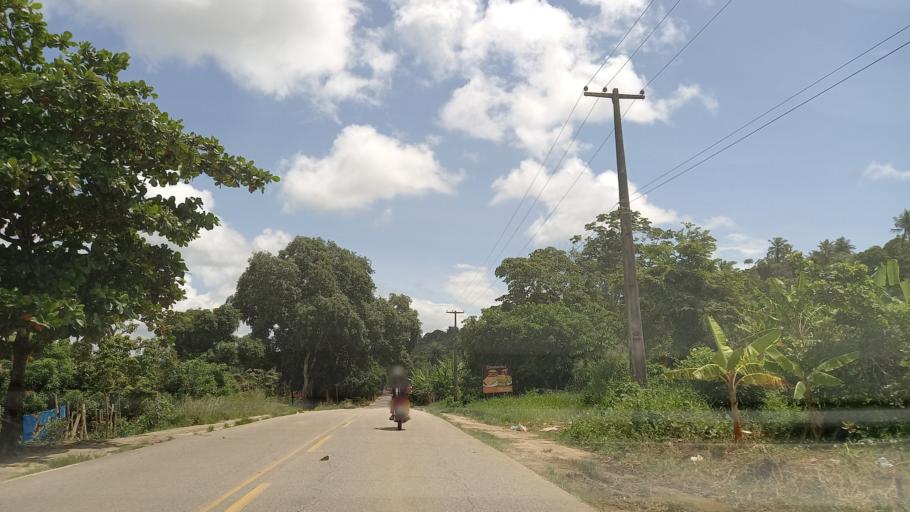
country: BR
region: Pernambuco
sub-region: Rio Formoso
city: Rio Formoso
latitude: -8.6559
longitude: -35.1491
